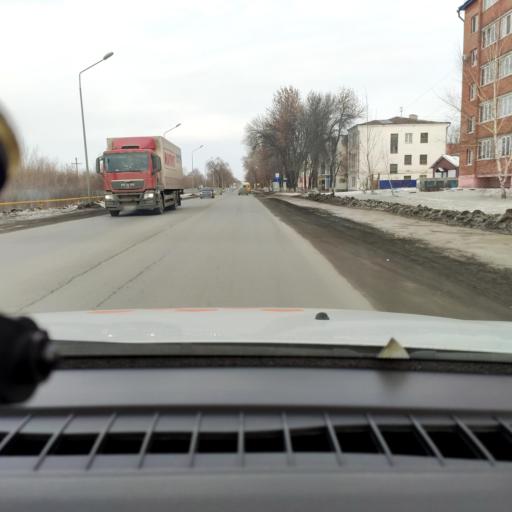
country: RU
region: Samara
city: Chapayevsk
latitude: 52.9708
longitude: 49.6986
